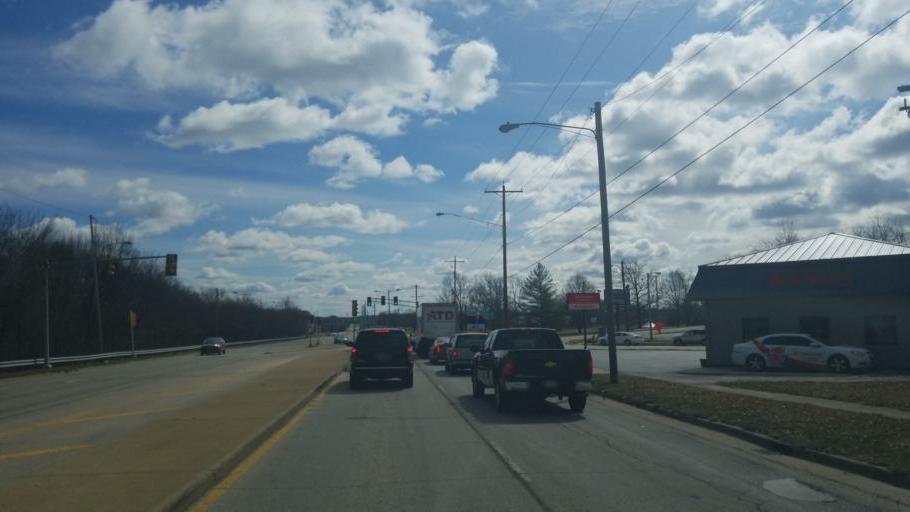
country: US
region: Illinois
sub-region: Macon County
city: Decatur
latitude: 39.8418
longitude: -88.9221
